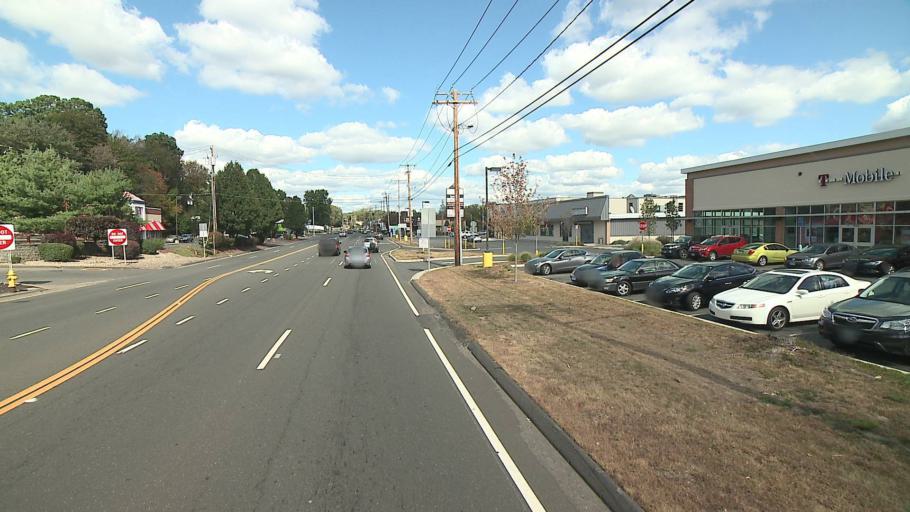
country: US
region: Connecticut
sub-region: New Haven County
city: Derby
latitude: 41.3314
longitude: -73.0845
